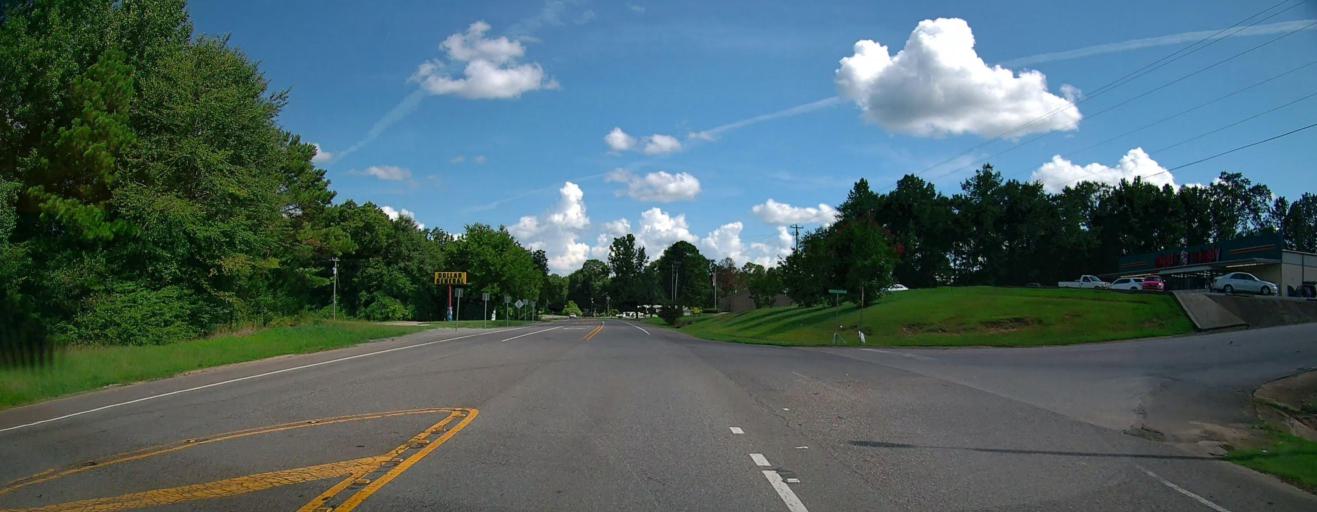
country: US
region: Alabama
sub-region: Pickens County
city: Gordo
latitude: 33.3224
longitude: -87.9099
